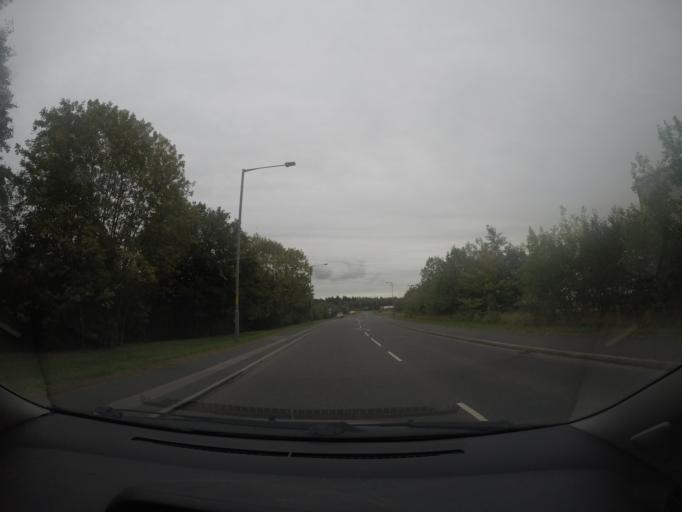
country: GB
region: England
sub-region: North Yorkshire
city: Barlby
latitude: 53.7767
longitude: -1.0427
